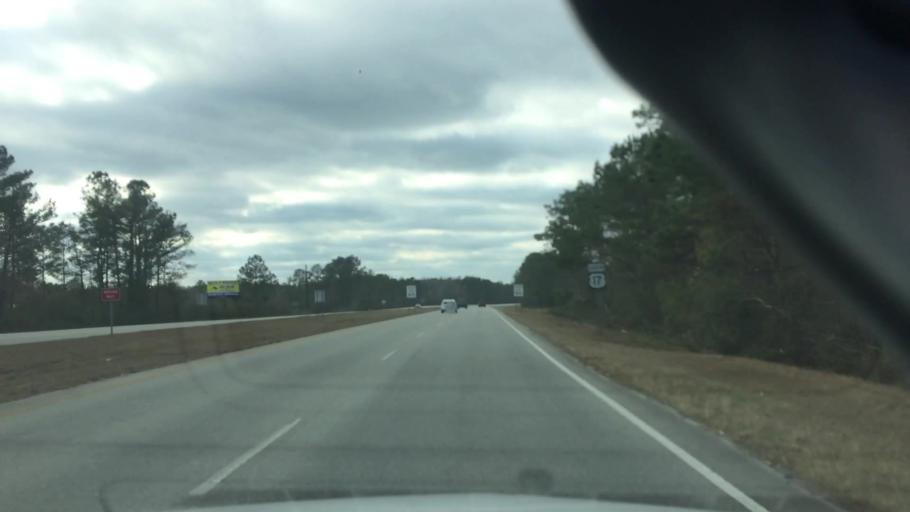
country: US
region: North Carolina
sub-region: Brunswick County
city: Bolivia
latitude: 34.0801
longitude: -78.1401
